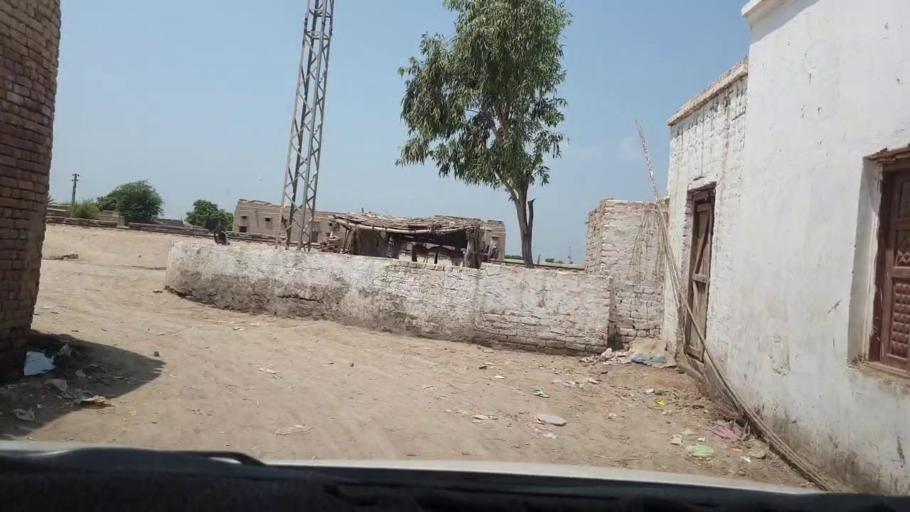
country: PK
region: Sindh
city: Radhan
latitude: 27.2466
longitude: 67.9887
